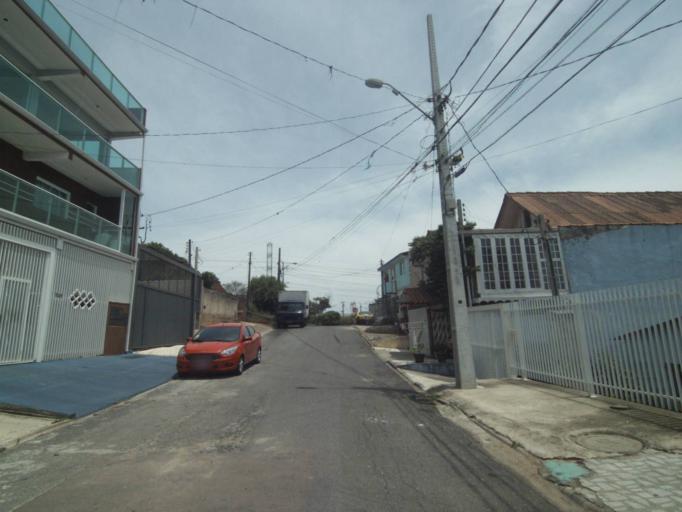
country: BR
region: Parana
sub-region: Curitiba
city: Curitiba
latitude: -25.5046
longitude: -49.3399
